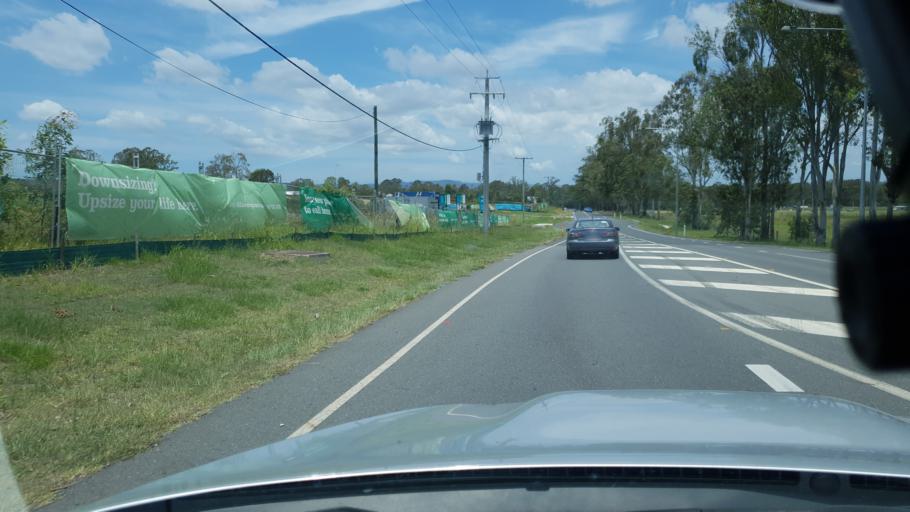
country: AU
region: Queensland
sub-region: Logan
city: North Maclean
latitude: -27.8243
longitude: 153.0100
